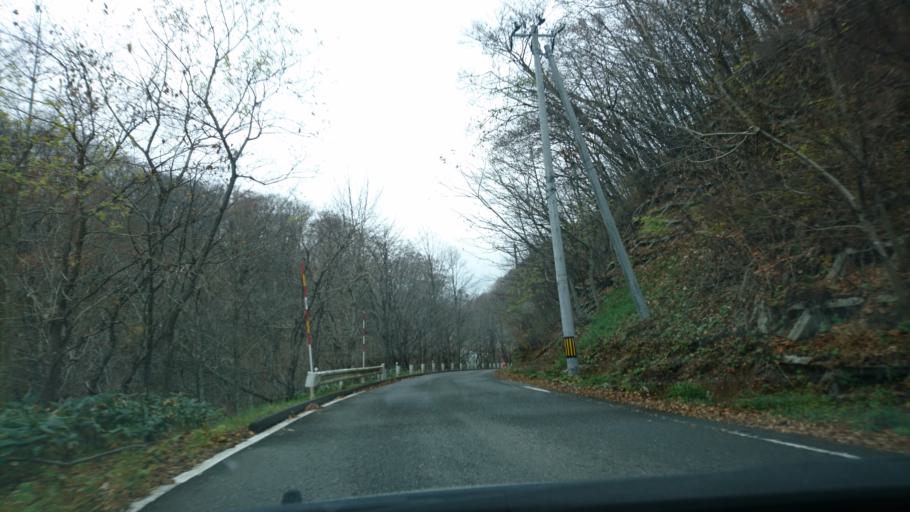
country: JP
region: Iwate
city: Ichinoseki
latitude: 38.9124
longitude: 140.8512
